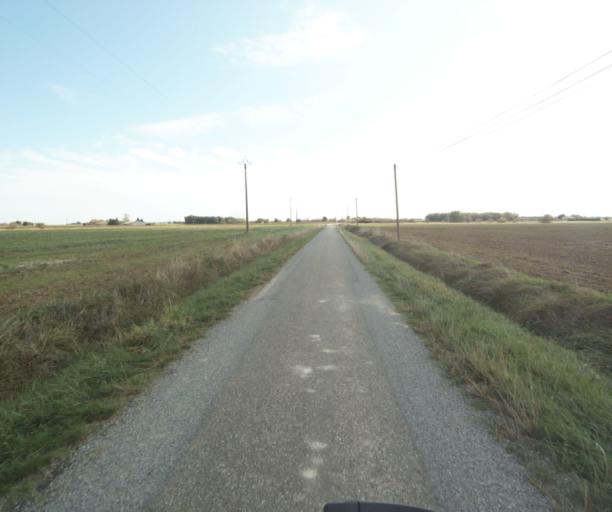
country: FR
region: Midi-Pyrenees
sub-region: Departement du Tarn-et-Garonne
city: Verdun-sur-Garonne
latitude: 43.8463
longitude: 1.1716
